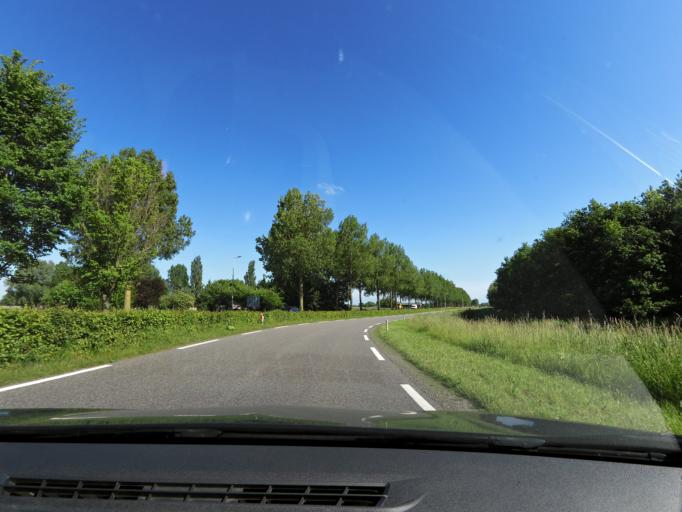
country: NL
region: South Holland
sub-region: Gemeente Hellevoetsluis
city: Nieuwenhoorn
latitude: 51.8604
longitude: 4.1575
